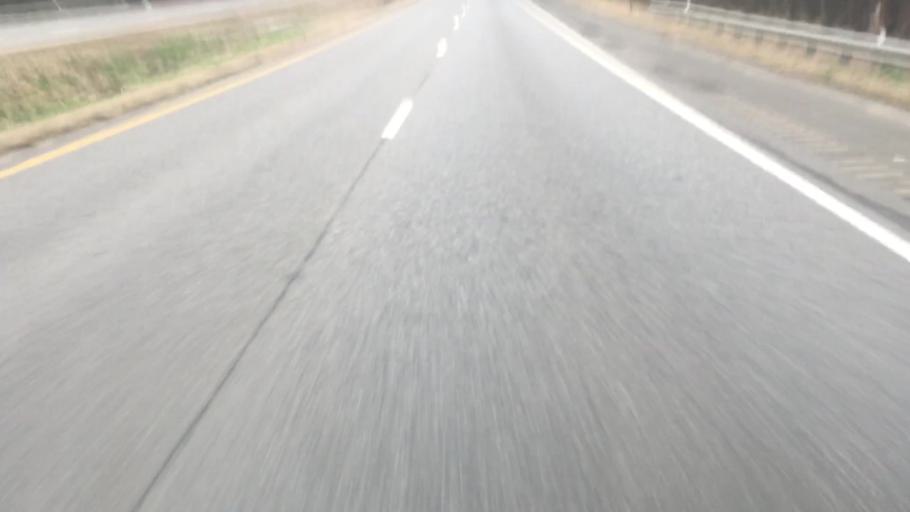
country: US
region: Alabama
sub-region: Jefferson County
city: Graysville
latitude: 33.6825
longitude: -86.9741
